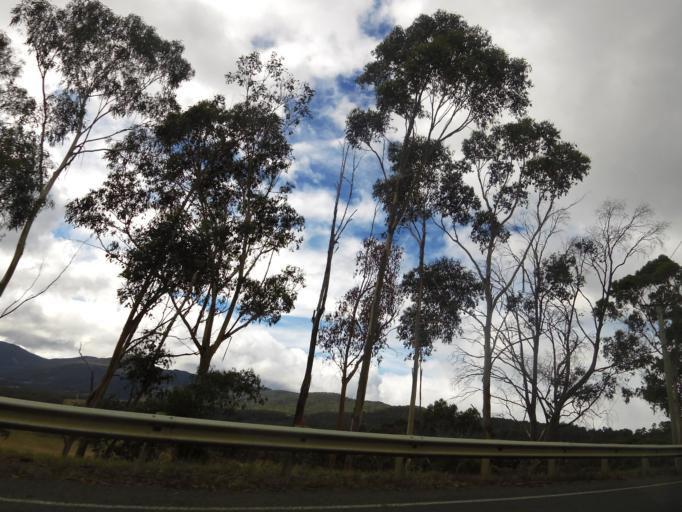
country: AU
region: Tasmania
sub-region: Huon Valley
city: Huonville
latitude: -42.9771
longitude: 147.1080
